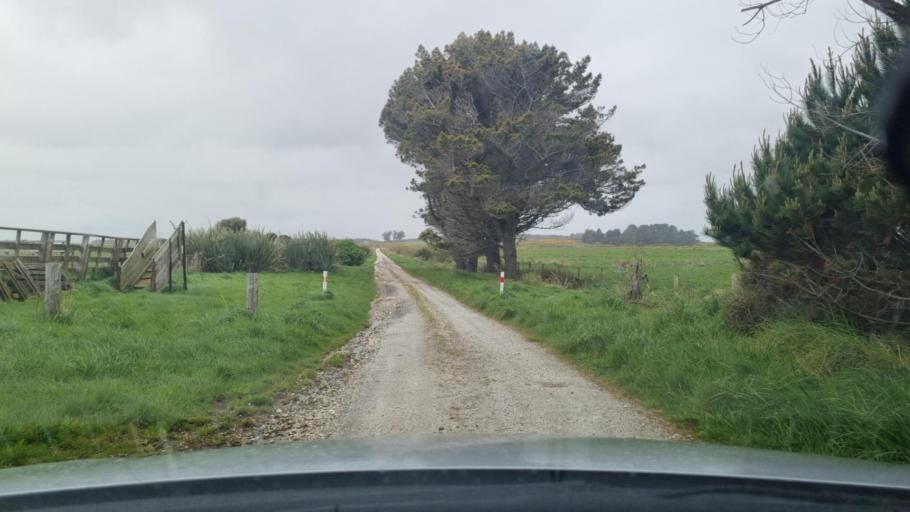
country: NZ
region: Southland
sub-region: Invercargill City
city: Bluff
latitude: -46.5202
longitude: 168.2736
